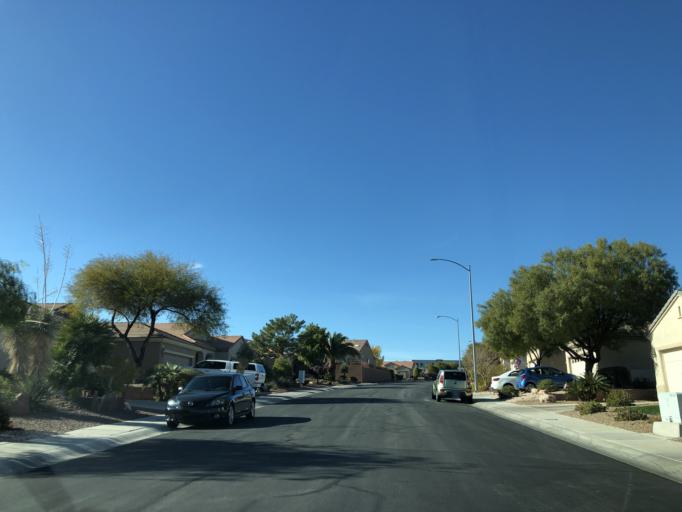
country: US
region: Nevada
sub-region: Clark County
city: Whitney
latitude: 36.0035
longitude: -115.0760
